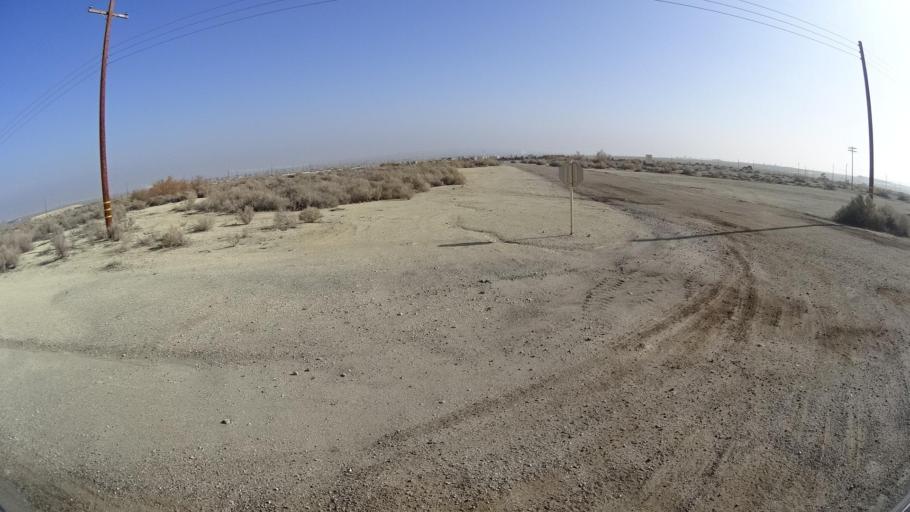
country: US
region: California
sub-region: Kern County
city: Taft Heights
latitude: 35.2050
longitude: -119.5693
